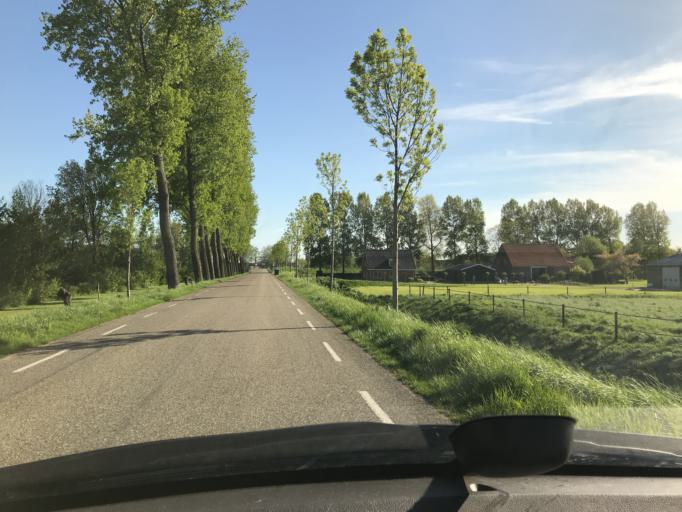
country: NL
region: Zeeland
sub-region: Gemeente Goes
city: Goes
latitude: 51.5572
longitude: 3.8105
